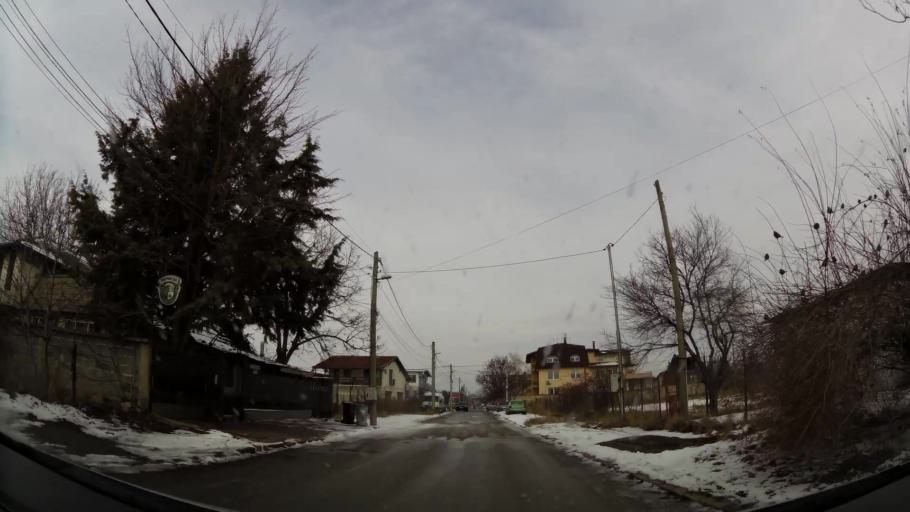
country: BG
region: Sofia-Capital
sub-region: Stolichna Obshtina
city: Sofia
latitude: 42.7094
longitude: 23.4125
